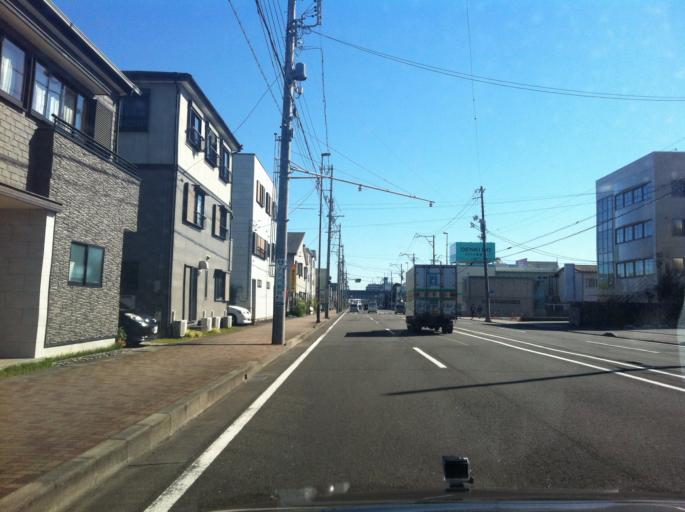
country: JP
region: Shizuoka
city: Shizuoka-shi
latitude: 34.9547
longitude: 138.4052
